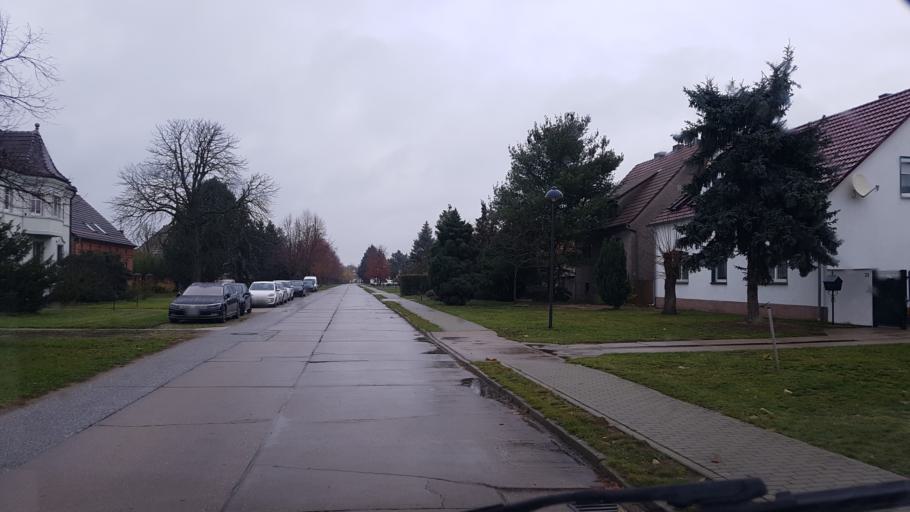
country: DE
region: Brandenburg
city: Herzberg
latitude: 51.6546
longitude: 13.2229
